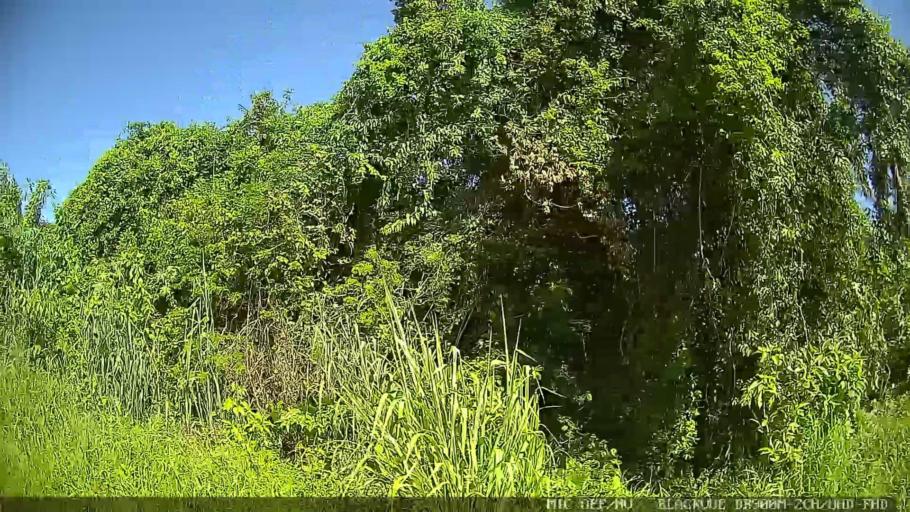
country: BR
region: Sao Paulo
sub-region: Iguape
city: Iguape
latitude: -24.6977
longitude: -47.5606
